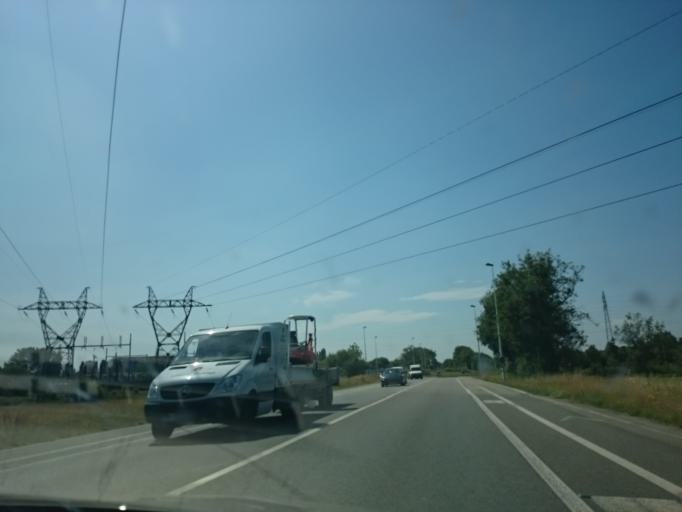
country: FR
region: Pays de la Loire
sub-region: Departement de la Loire-Atlantique
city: Indre
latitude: 47.2066
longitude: -1.6821
